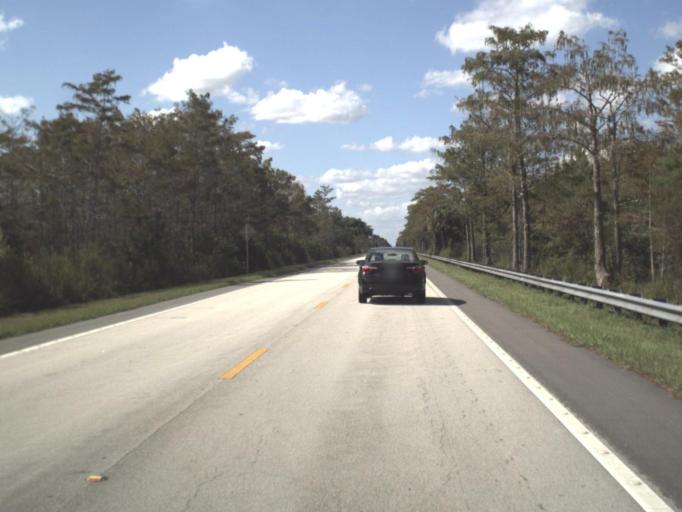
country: US
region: Florida
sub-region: Miami-Dade County
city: Kendall West
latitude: 25.8155
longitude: -80.8848
